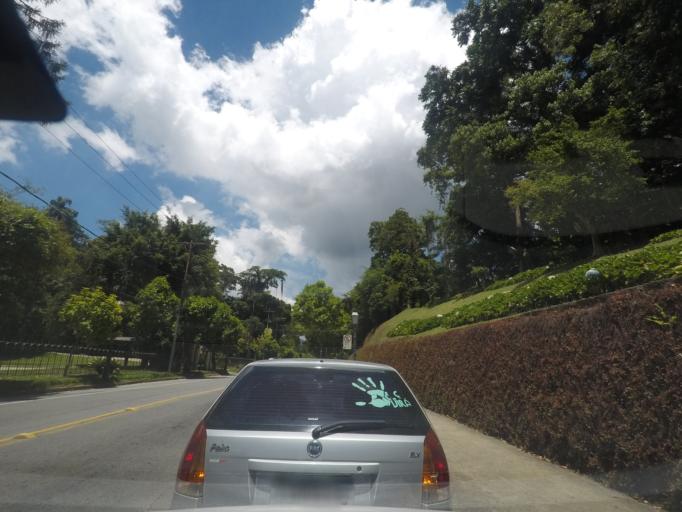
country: BR
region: Rio de Janeiro
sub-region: Petropolis
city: Petropolis
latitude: -22.5033
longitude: -43.1731
